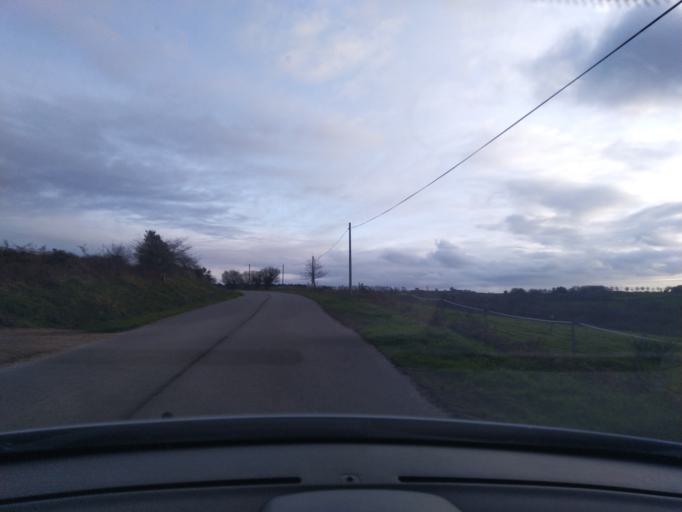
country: FR
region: Brittany
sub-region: Departement du Finistere
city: Guerlesquin
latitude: 48.5258
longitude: -3.6033
